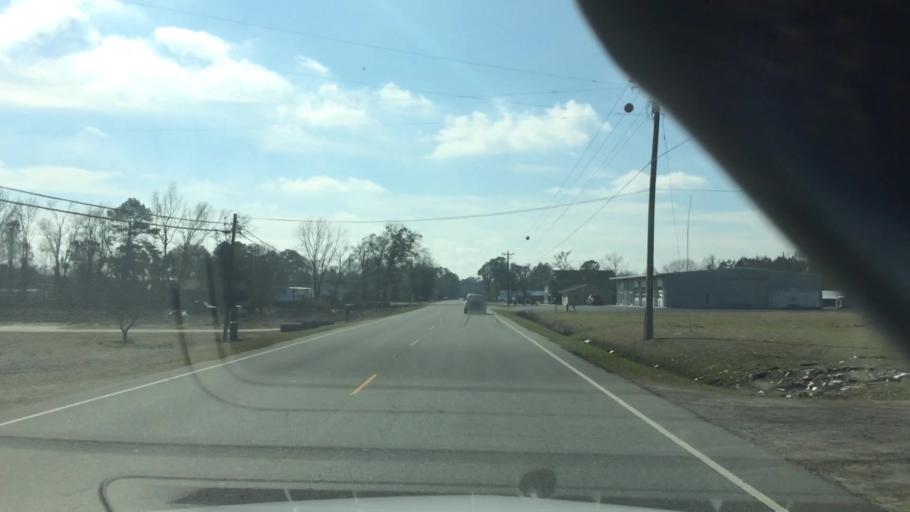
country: US
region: North Carolina
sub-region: Duplin County
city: Wallace
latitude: 34.7824
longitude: -77.9090
